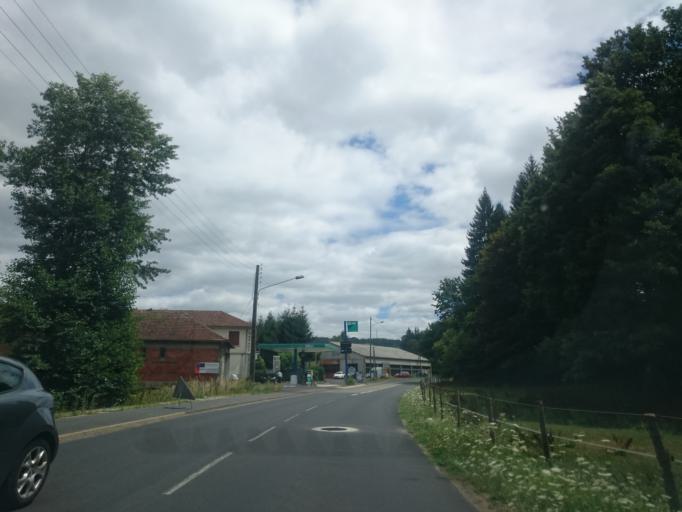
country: FR
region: Auvergne
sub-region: Departement du Cantal
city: Laroquebrou
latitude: 44.9679
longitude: 2.2003
